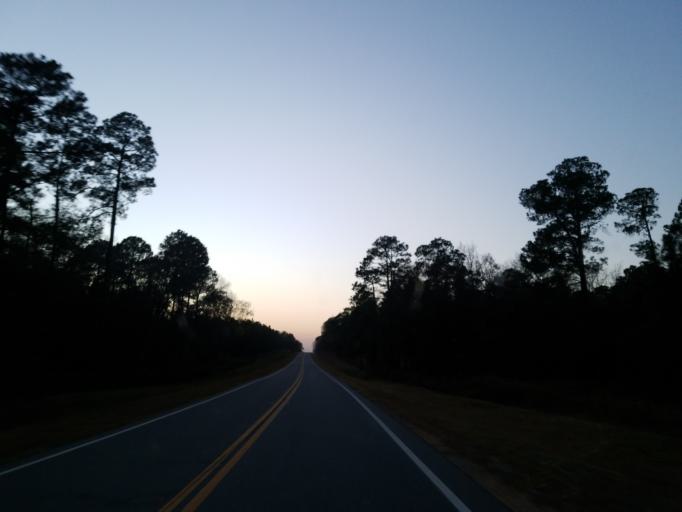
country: US
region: Georgia
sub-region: Turner County
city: Ashburn
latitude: 31.8239
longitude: -83.5501
